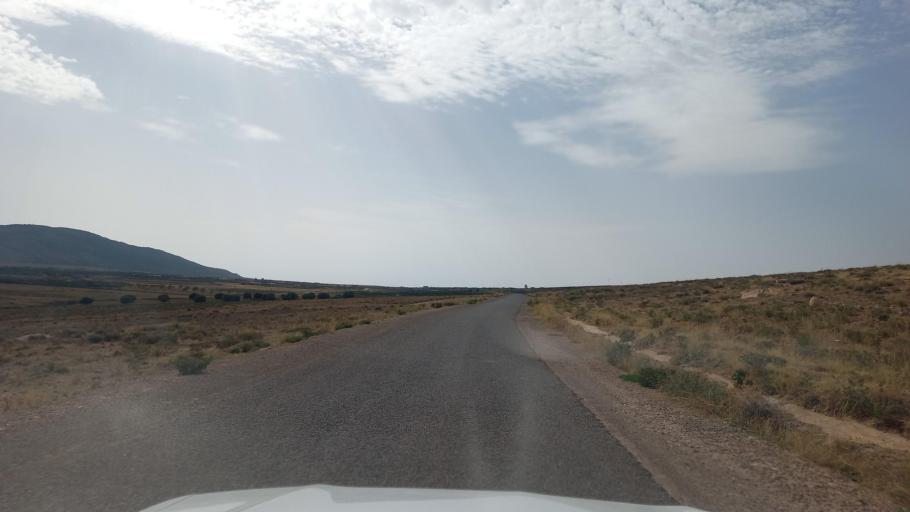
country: TN
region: Al Qasrayn
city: Kasserine
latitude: 35.3600
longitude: 8.8370
